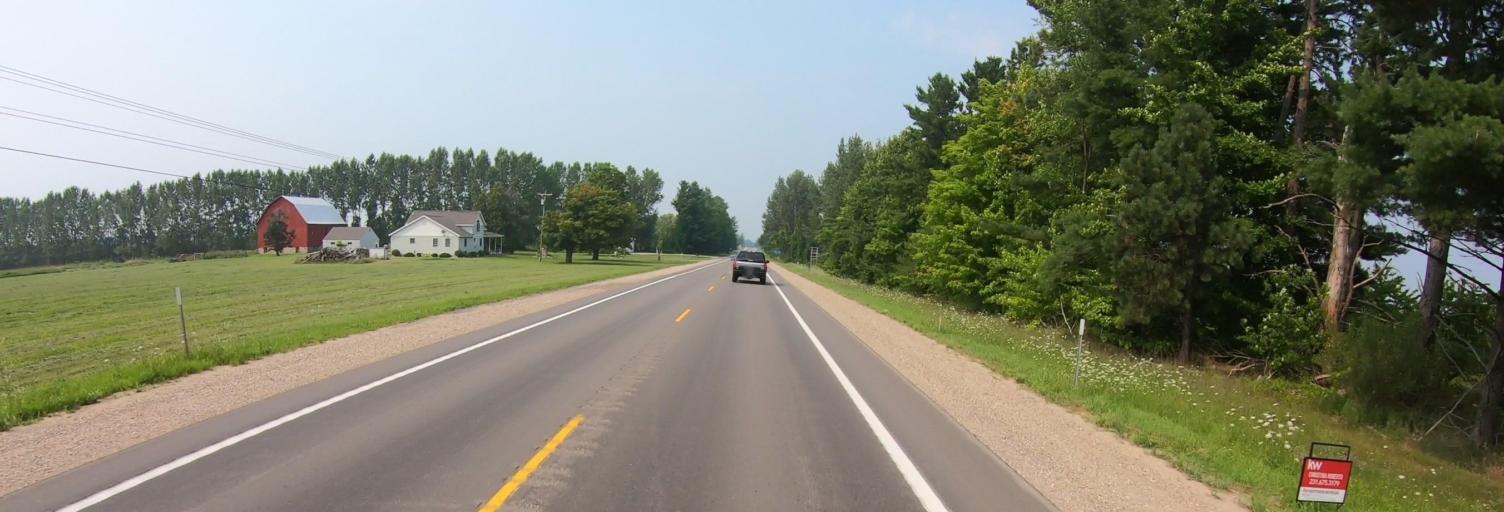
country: US
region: Michigan
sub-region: Antrim County
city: Elk Rapids
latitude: 45.0144
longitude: -85.3527
